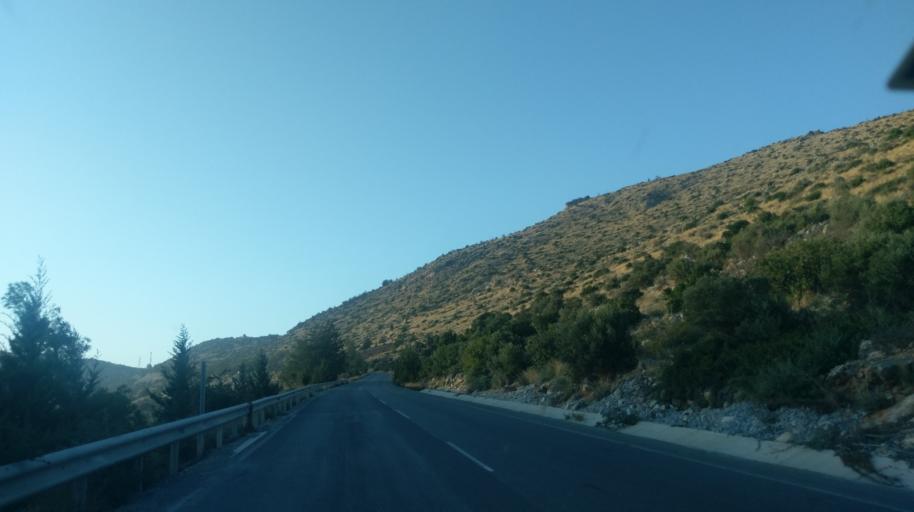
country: CY
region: Lefkosia
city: Nicosia
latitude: 35.2752
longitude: 33.4806
